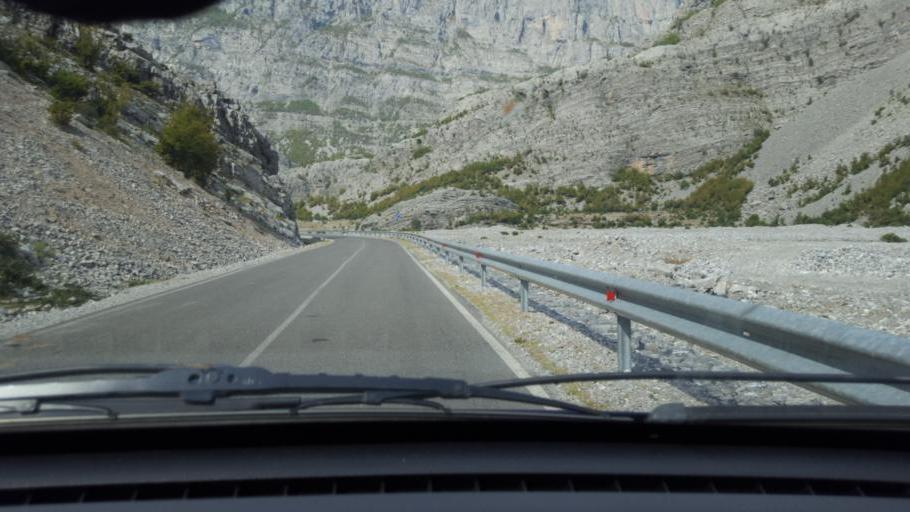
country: AL
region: Shkoder
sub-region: Rrethi i Malesia e Madhe
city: Kastrat
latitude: 42.4880
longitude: 19.5844
